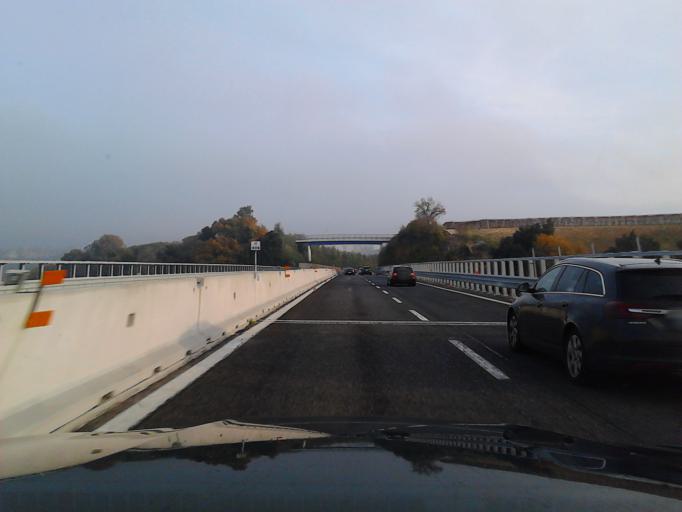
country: IT
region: Abruzzo
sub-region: Provincia di Chieti
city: San Vito Chietino
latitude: 42.2996
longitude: 14.4272
